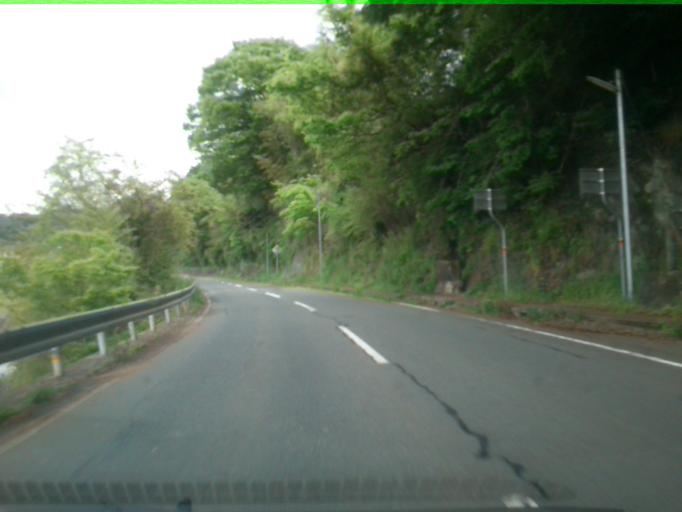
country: JP
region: Kyoto
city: Ayabe
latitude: 35.2716
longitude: 135.3977
